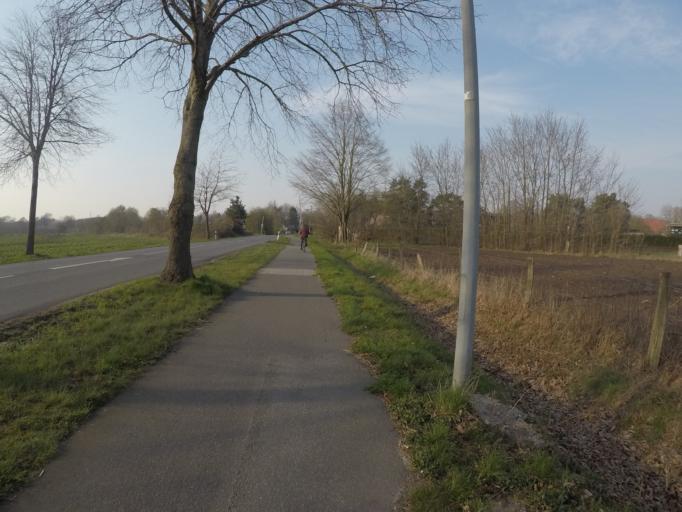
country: DE
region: Schleswig-Holstein
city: Rickling
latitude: 53.9954
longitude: 10.1735
